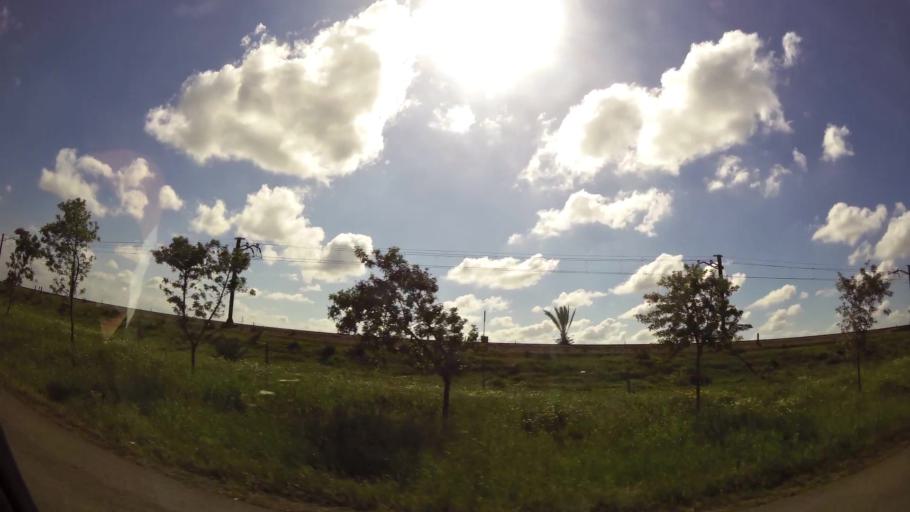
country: MA
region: Chaouia-Ouardigha
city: Nouaseur
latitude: 33.4054
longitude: -7.6241
